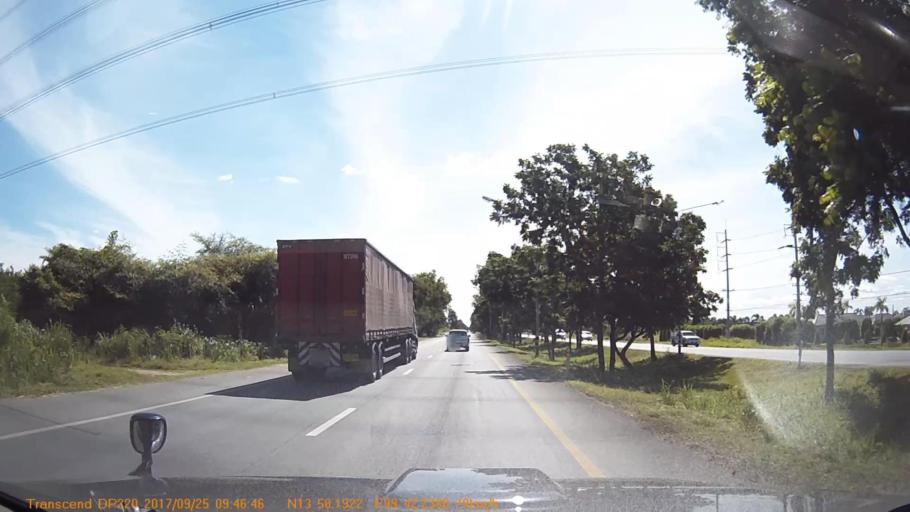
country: TH
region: Kanchanaburi
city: Tha Muang
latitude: 13.9698
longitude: 99.7045
